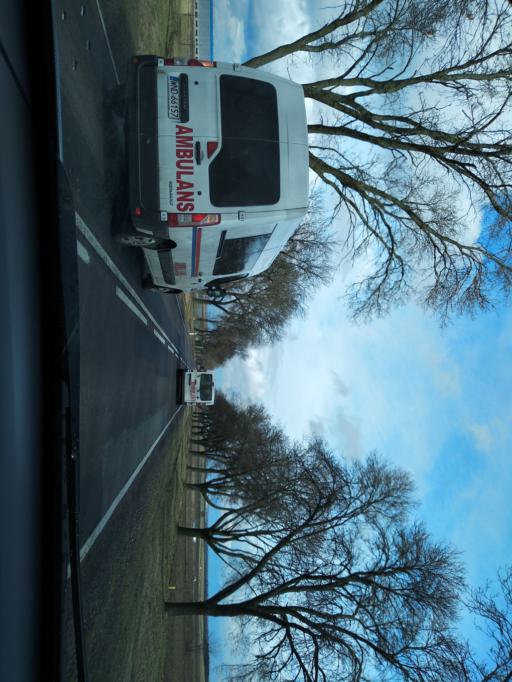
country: PL
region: Lodz Voivodeship
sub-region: Powiat zgierski
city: Strykow
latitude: 51.8689
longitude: 19.5220
